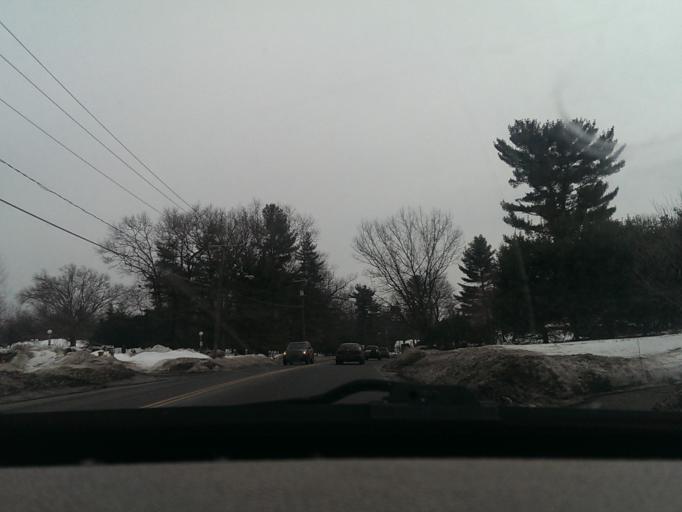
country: US
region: Massachusetts
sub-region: Hampden County
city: Longmeadow
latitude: 42.0646
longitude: -72.5524
